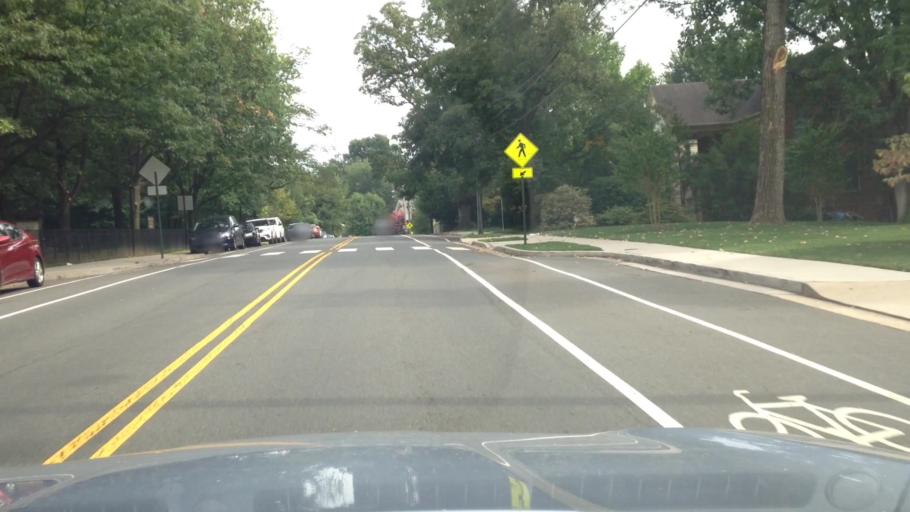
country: US
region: Virginia
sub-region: Fairfax County
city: Seven Corners
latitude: 38.9007
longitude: -77.1431
